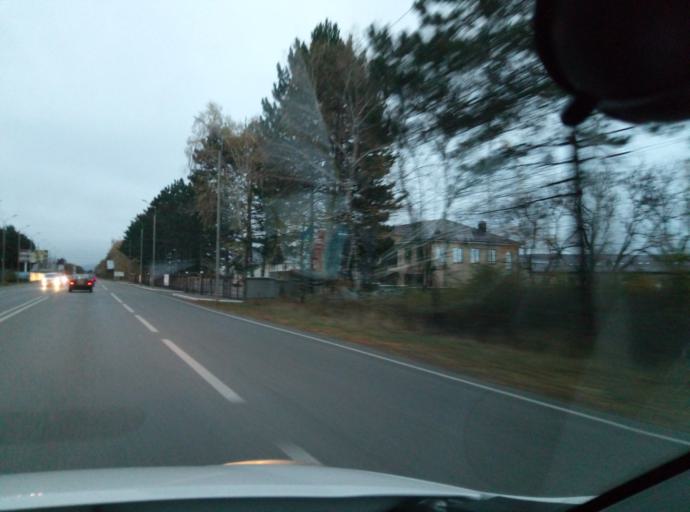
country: RU
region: Stavropol'skiy
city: Yessentukskaya
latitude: 44.0545
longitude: 42.9204
